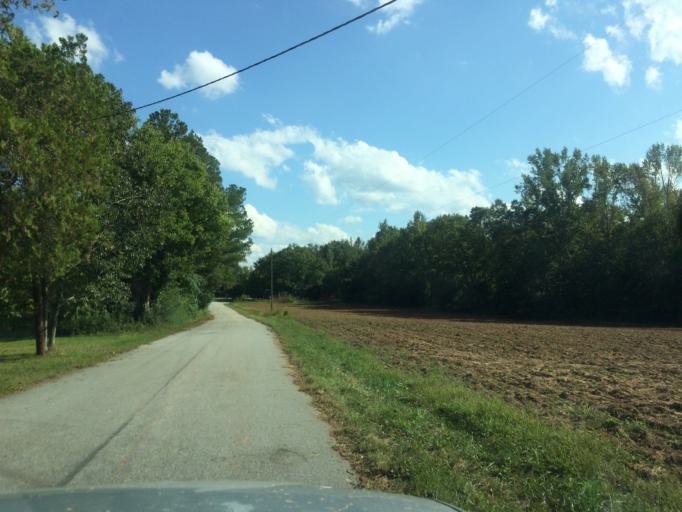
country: US
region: South Carolina
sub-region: Greenwood County
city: Ware Shoals
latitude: 34.4587
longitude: -82.1744
